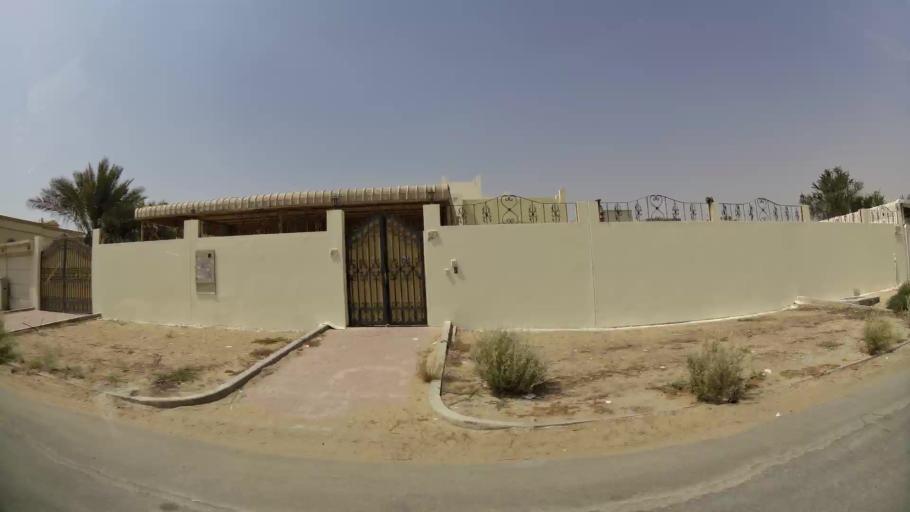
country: AE
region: Ash Shariqah
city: Sharjah
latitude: 25.2390
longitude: 55.4314
